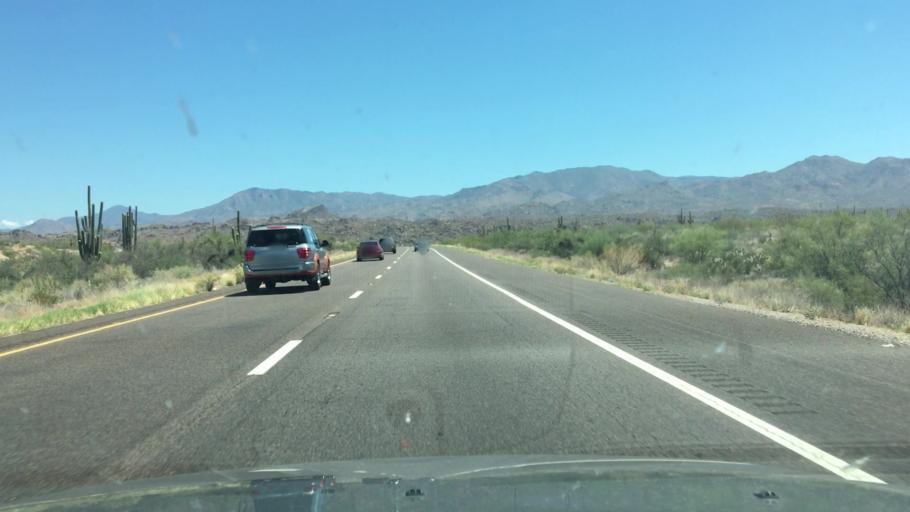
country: US
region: Arizona
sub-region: Maricopa County
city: Rio Verde
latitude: 33.6646
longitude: -111.5136
